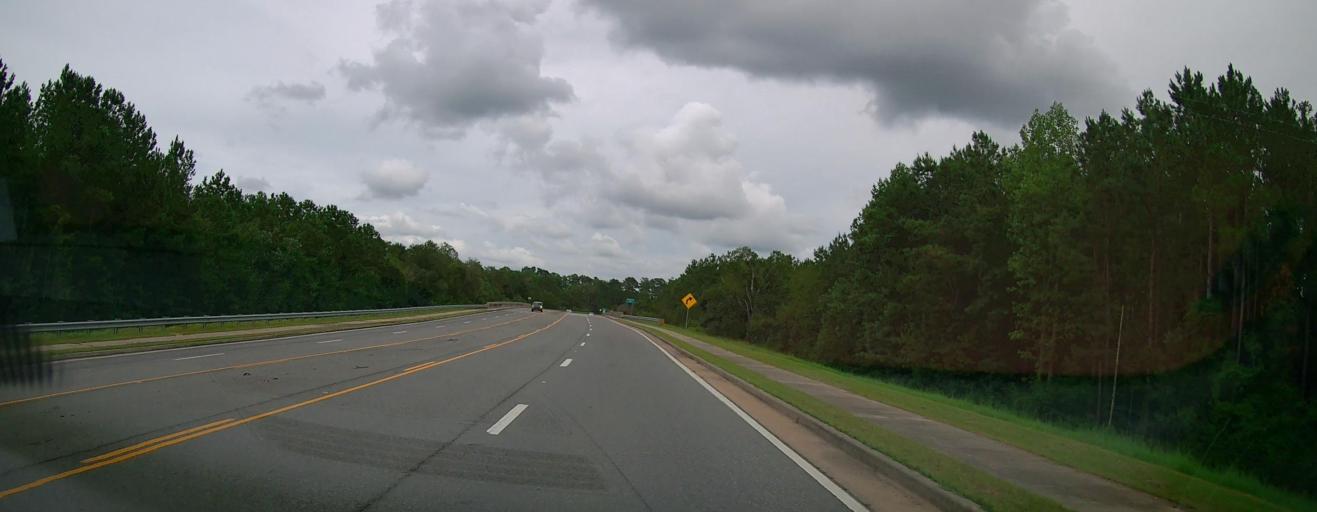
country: US
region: Georgia
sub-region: Wayne County
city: Jesup
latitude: 31.6677
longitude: -82.0430
